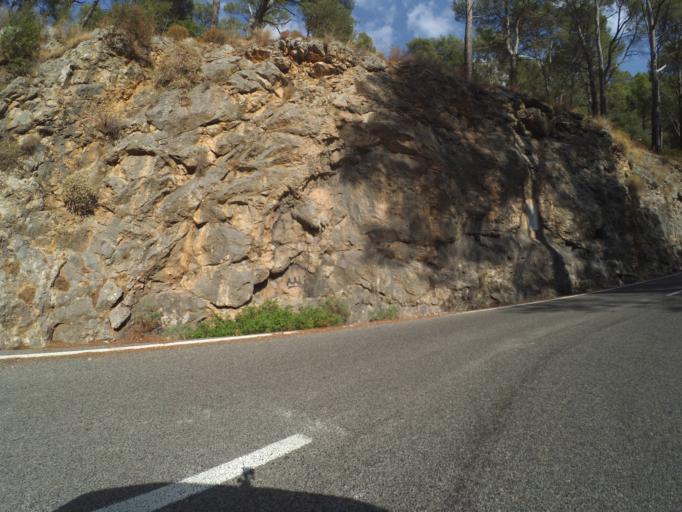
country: ES
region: Balearic Islands
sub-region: Illes Balears
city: Selva
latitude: 39.7784
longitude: 2.8983
